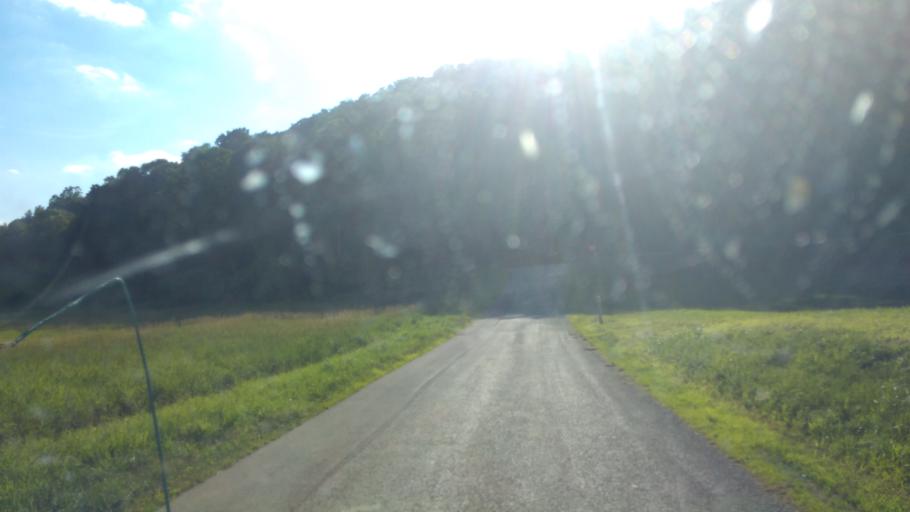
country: US
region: Ohio
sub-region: Ashland County
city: Loudonville
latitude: 40.7337
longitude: -82.1481
